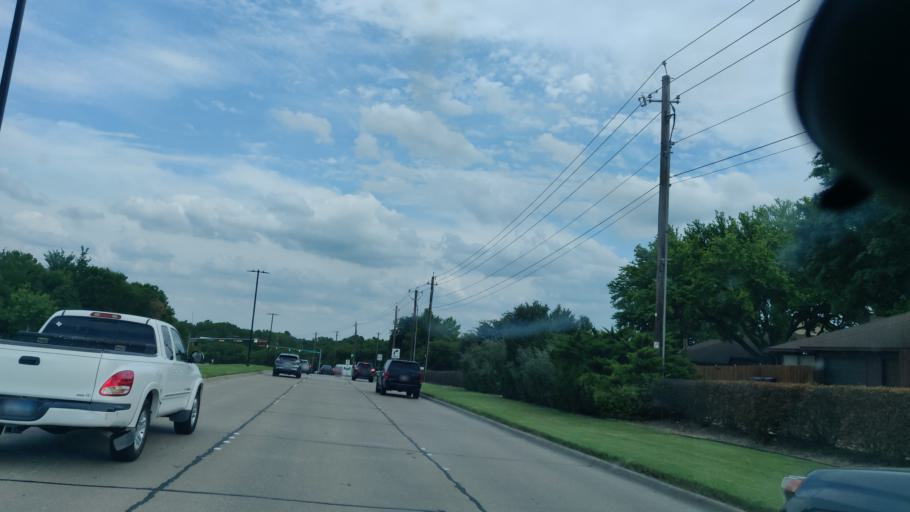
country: US
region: Texas
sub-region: Dallas County
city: Sachse
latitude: 32.9328
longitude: -96.5982
